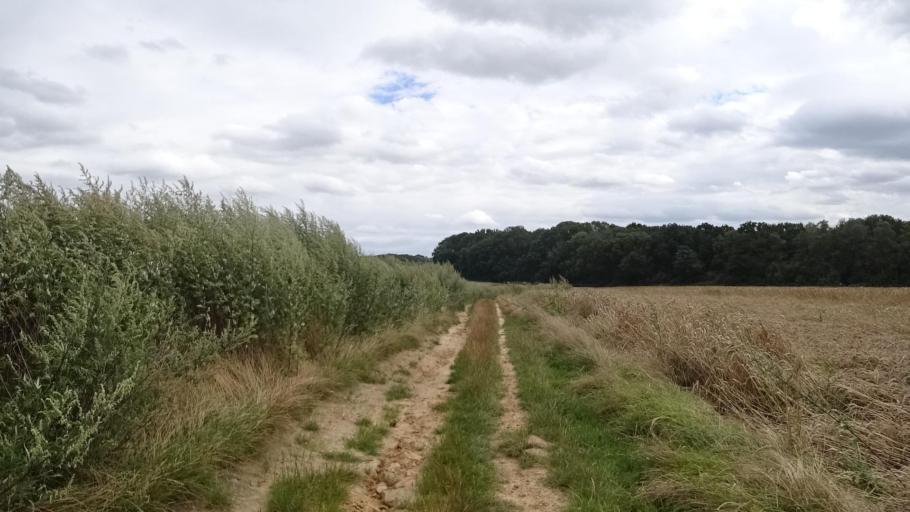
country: BE
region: Wallonia
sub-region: Province du Brabant Wallon
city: Mont-Saint-Guibert
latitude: 50.6453
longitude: 4.6171
